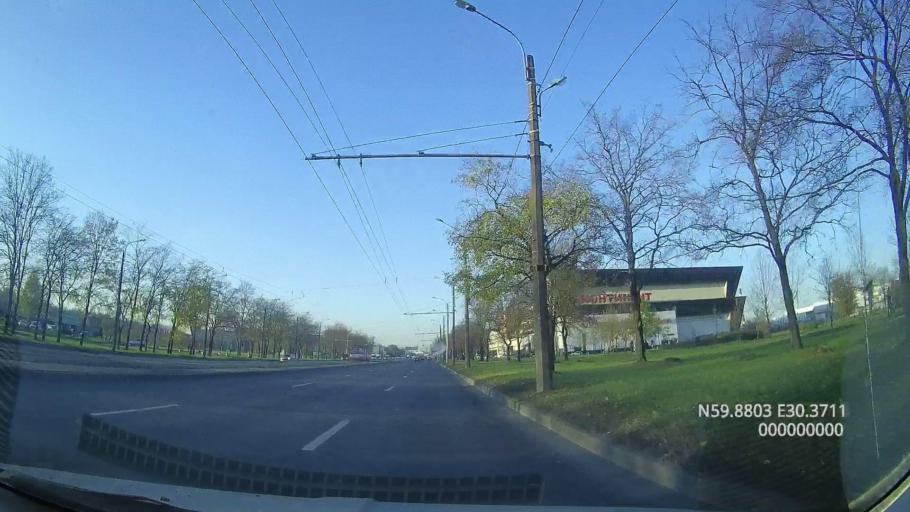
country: RU
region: St.-Petersburg
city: Kupchino
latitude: 59.8829
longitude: 30.3699
